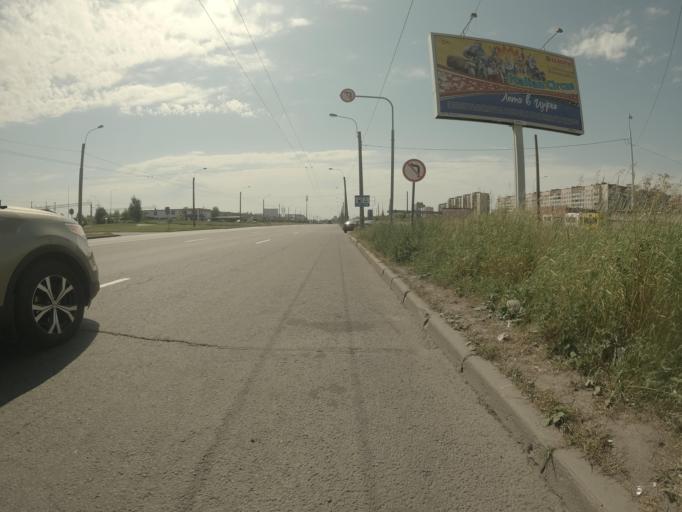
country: RU
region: St.-Petersburg
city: Krasnogvargeisky
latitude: 59.9422
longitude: 30.5047
